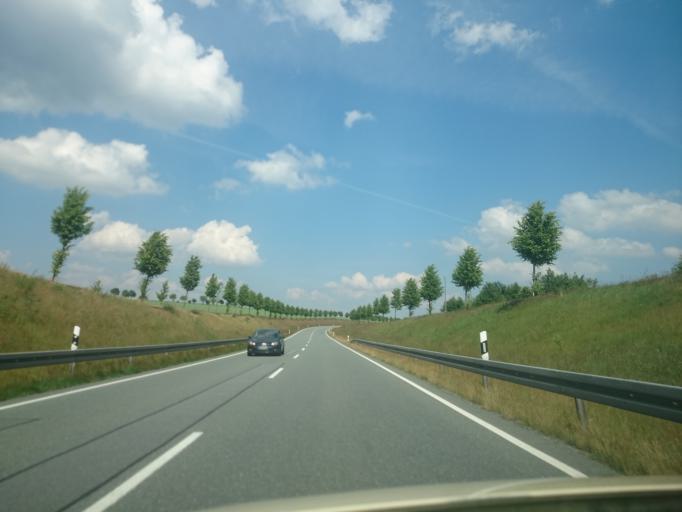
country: DE
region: Saxony
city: Marienberg
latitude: 50.6697
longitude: 13.1460
